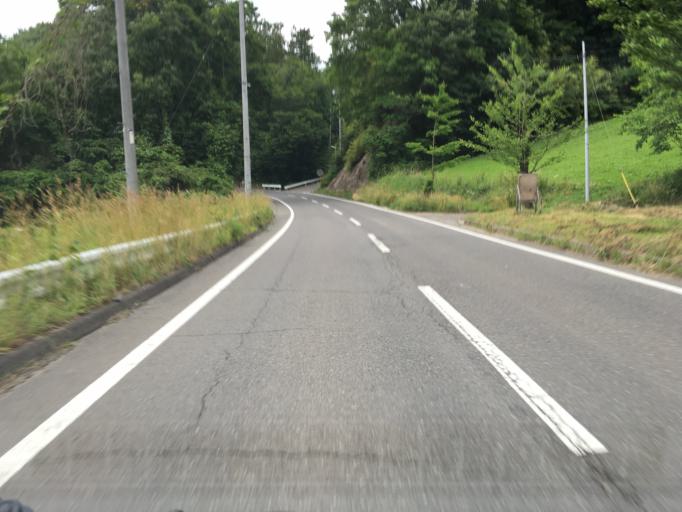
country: JP
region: Fukushima
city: Nihommatsu
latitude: 37.6281
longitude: 140.5400
